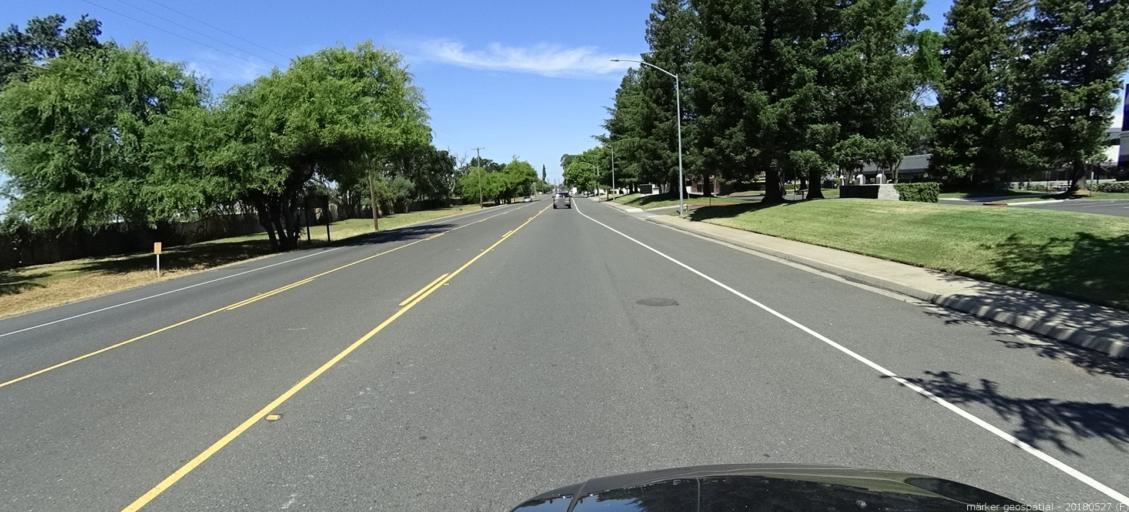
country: US
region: California
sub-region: Sacramento County
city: Rosemont
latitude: 38.5449
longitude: -121.3926
